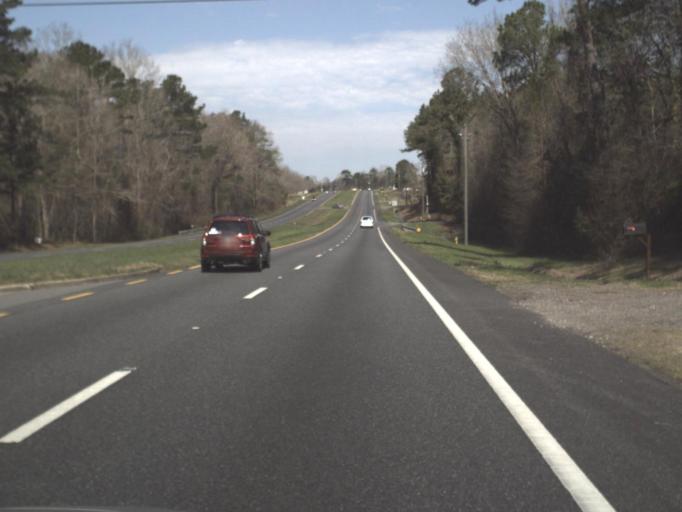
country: US
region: Florida
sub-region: Gadsden County
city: Havana
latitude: 30.5823
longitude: -84.4004
